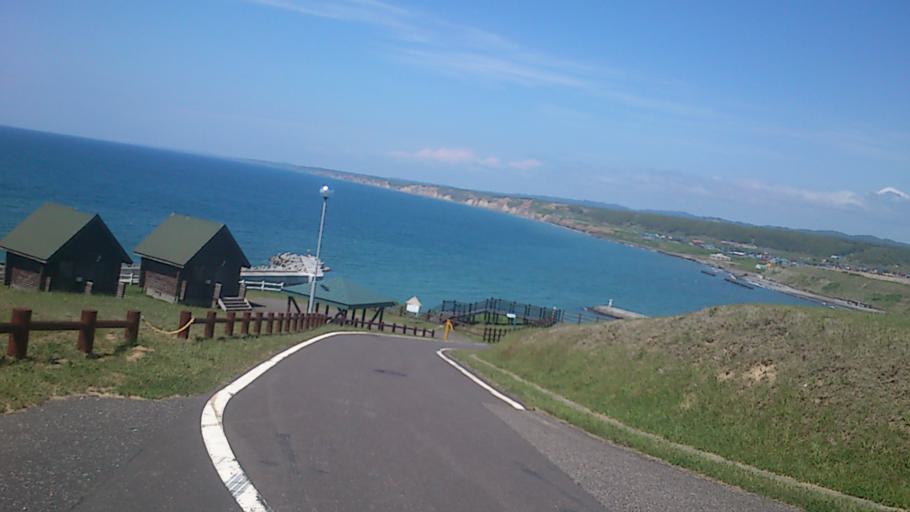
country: JP
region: Hokkaido
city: Rumoi
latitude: 44.5632
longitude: 141.7738
